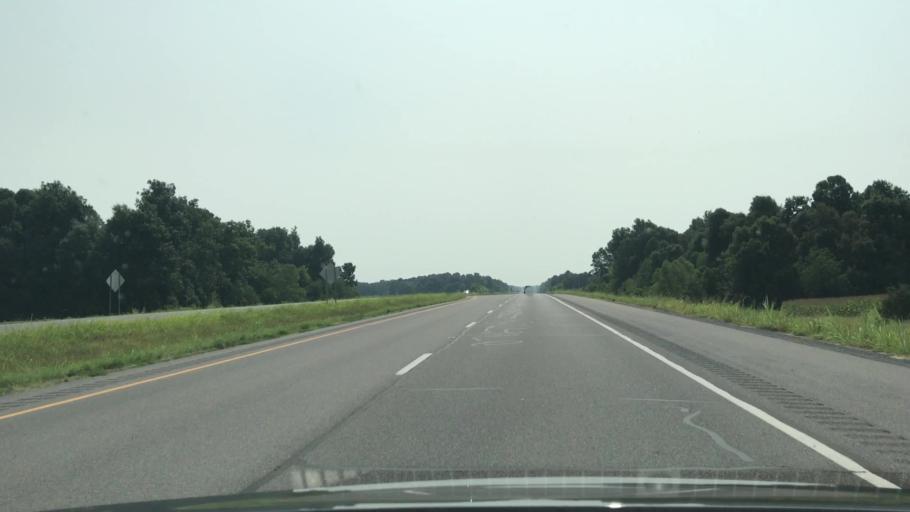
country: US
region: Kentucky
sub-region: Graves County
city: Mayfield
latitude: 36.6768
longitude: -88.5214
